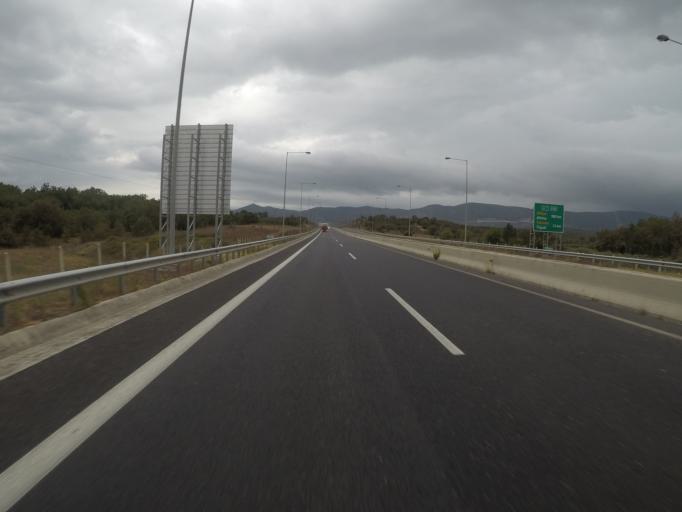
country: GR
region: Peloponnese
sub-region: Nomos Arkadias
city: Megalopoli
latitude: 37.3681
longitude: 22.1543
